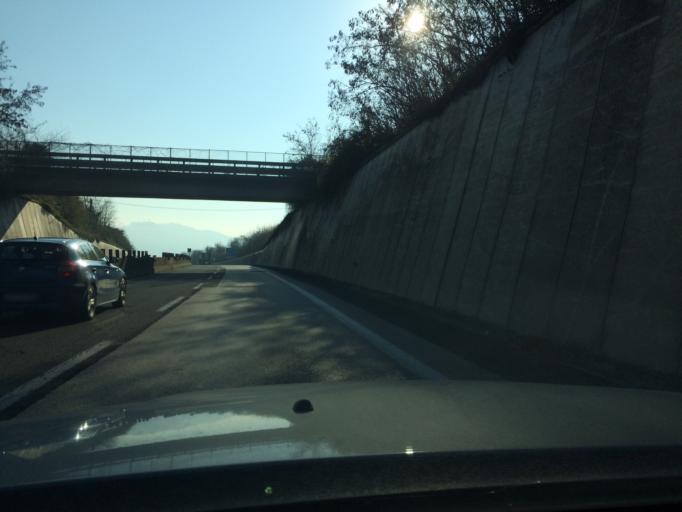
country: IT
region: Umbria
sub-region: Provincia di Perugia
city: Ponterio-Pian di Porto
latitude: 42.8261
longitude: 12.3988
